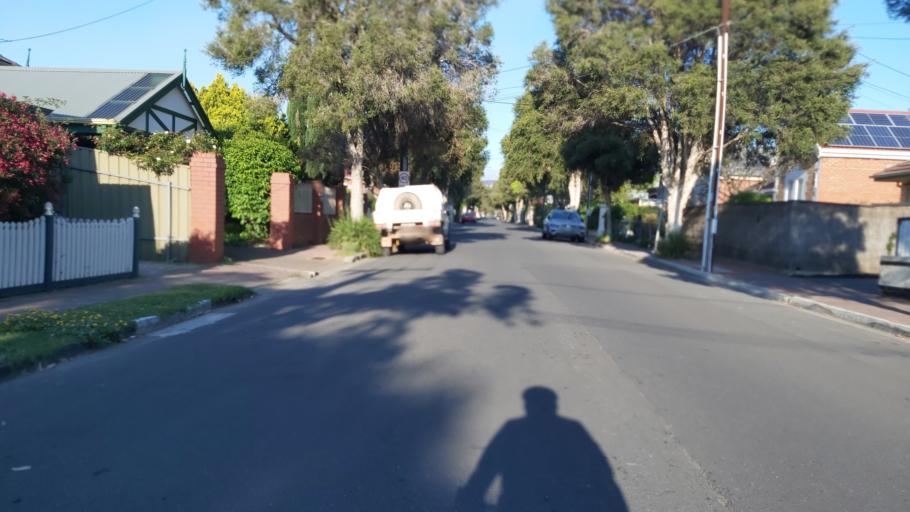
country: AU
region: South Australia
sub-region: Unley
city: Fullarton
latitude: -34.9462
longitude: 138.6159
